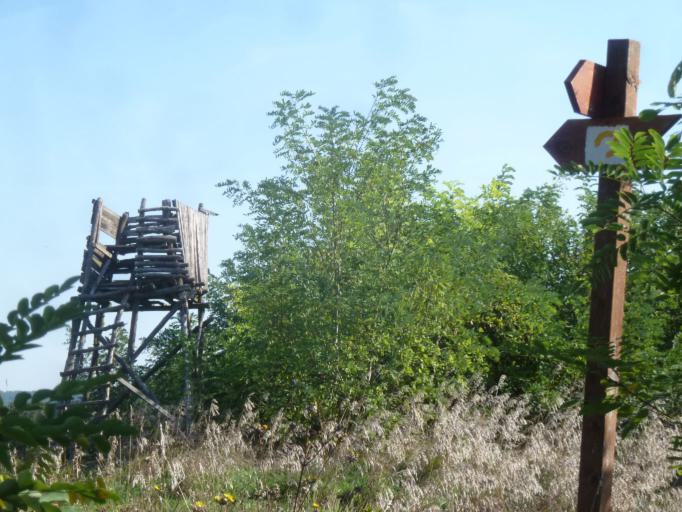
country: HU
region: Nograd
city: Romhany
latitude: 47.8826
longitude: 19.3179
